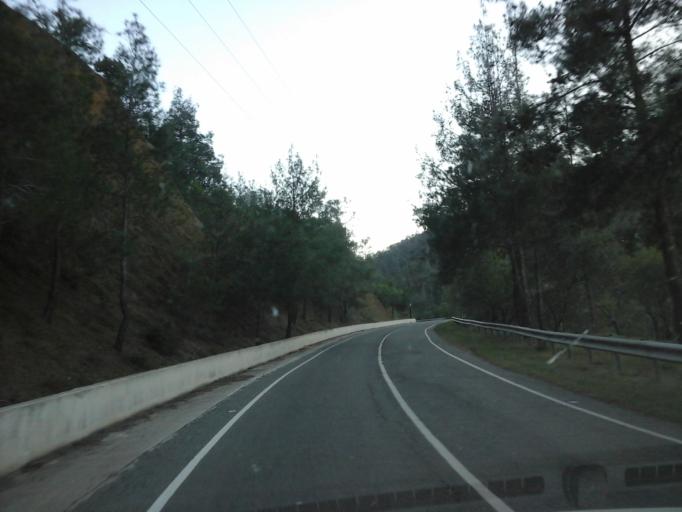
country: CY
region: Lefkosia
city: Astromeritis
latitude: 35.0611
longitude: 32.9881
